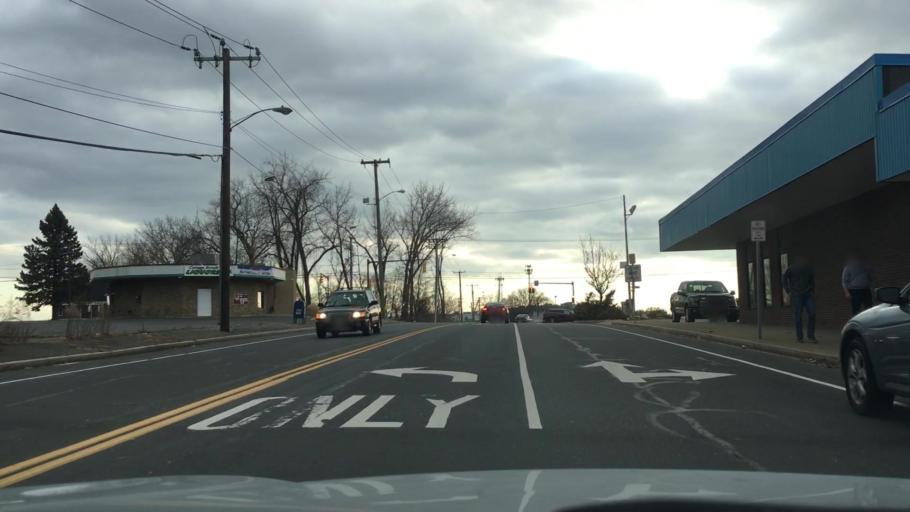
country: US
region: Massachusetts
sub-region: Hampden County
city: Springfield
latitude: 42.1451
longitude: -72.5434
